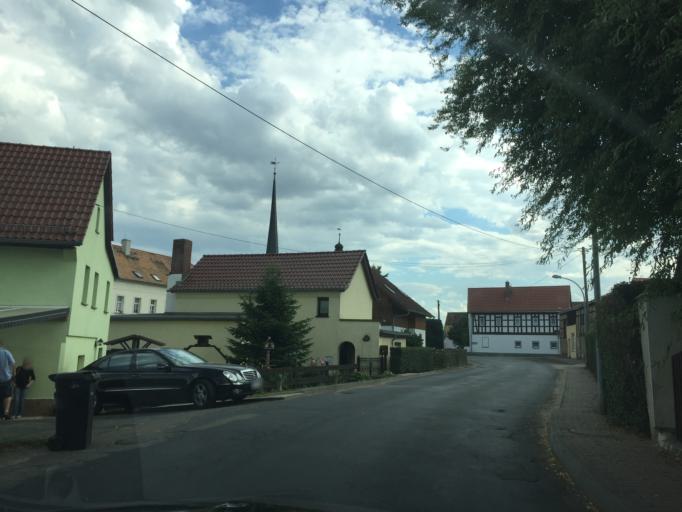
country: DE
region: Thuringia
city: Saara
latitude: 50.9533
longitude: 12.4305
